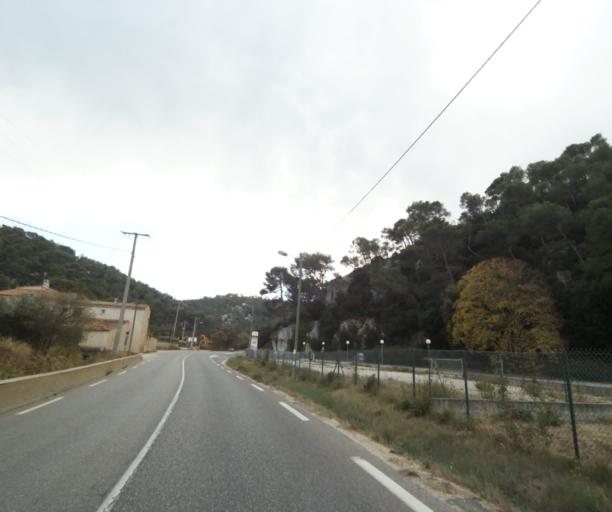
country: FR
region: Provence-Alpes-Cote d'Azur
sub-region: Departement des Bouches-du-Rhone
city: Gemenos
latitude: 43.2700
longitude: 5.6463
